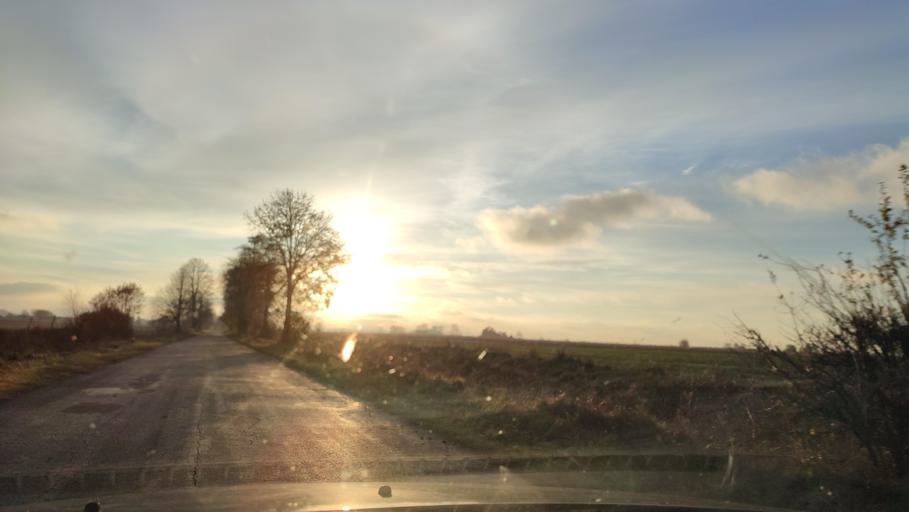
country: PL
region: Masovian Voivodeship
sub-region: Powiat mlawski
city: Dzierzgowo
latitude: 53.2522
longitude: 20.5901
